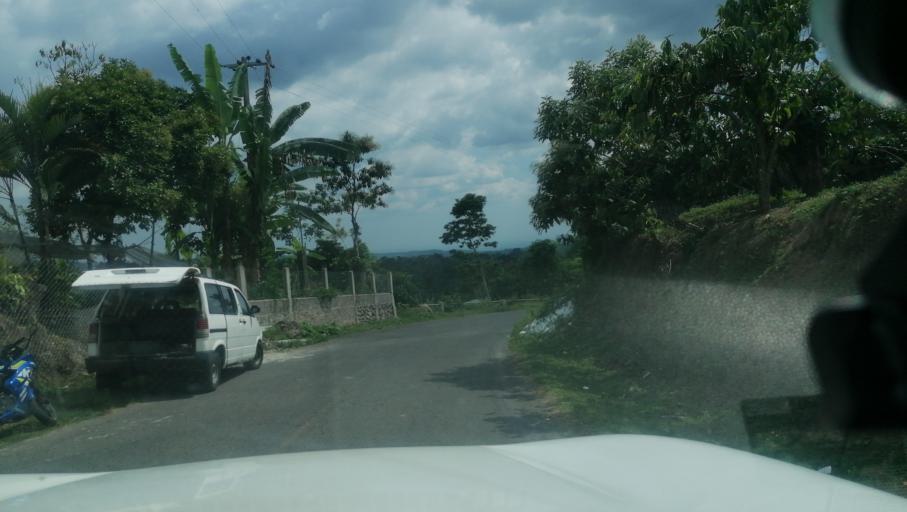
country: MX
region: Chiapas
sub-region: Cacahoatan
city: Benito Juarez
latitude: 15.0439
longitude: -92.1515
